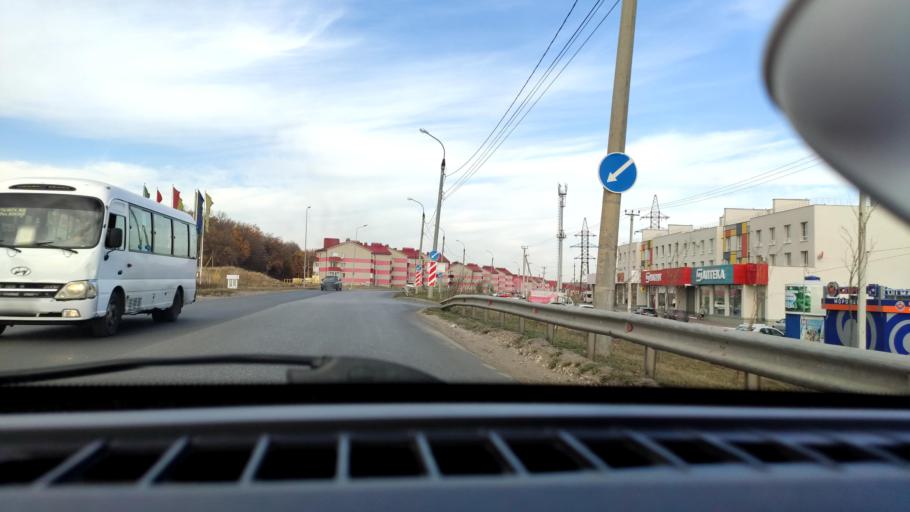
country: RU
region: Samara
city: Novosemeykino
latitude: 53.3267
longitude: 50.3109
